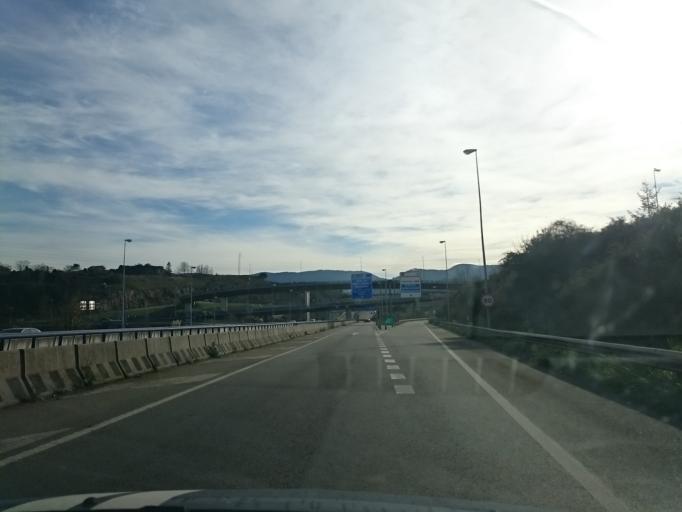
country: ES
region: Asturias
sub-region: Province of Asturias
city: Gijon
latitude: 43.5194
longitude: -5.6579
